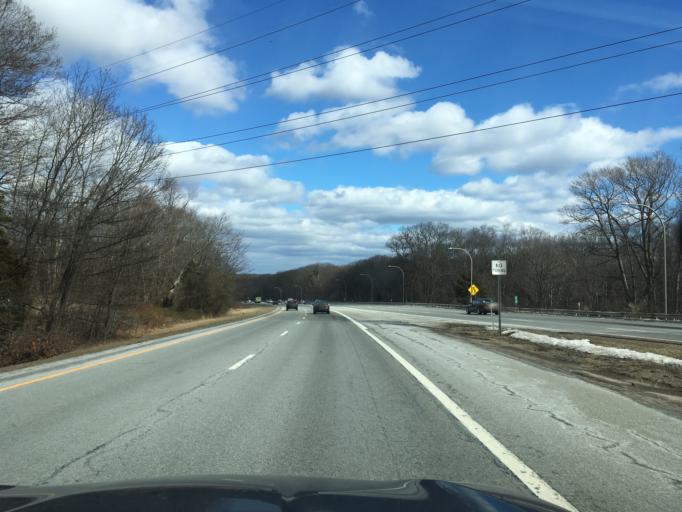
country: US
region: Rhode Island
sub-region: Kent County
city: East Greenwich
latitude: 41.6673
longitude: -71.4871
